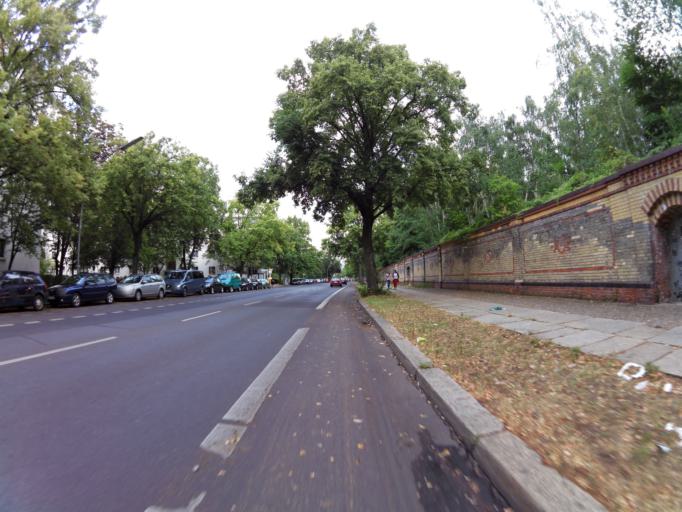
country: DE
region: Berlin
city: Gesundbrunnen
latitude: 52.5356
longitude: 13.3848
